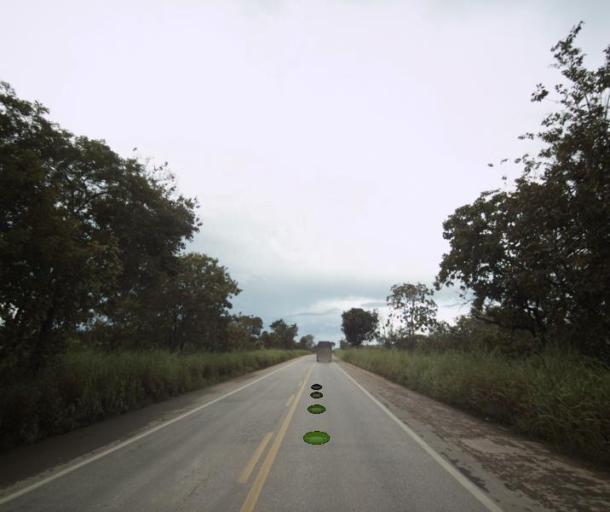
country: BR
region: Goias
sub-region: Porangatu
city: Porangatu
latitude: -13.5718
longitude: -49.0464
